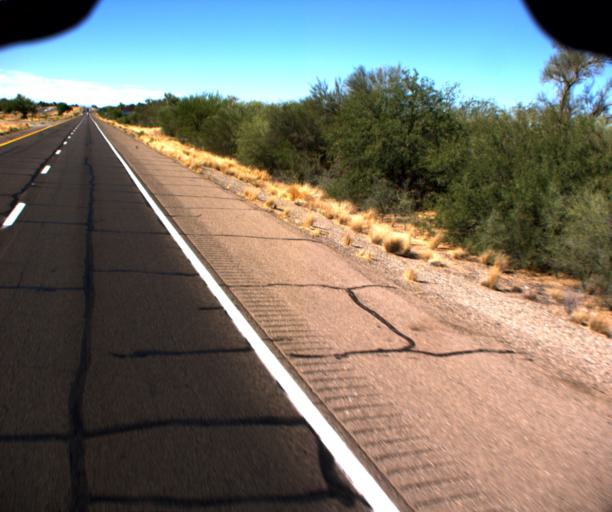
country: US
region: Arizona
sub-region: Pima County
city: Green Valley
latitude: 31.8622
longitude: -110.9920
